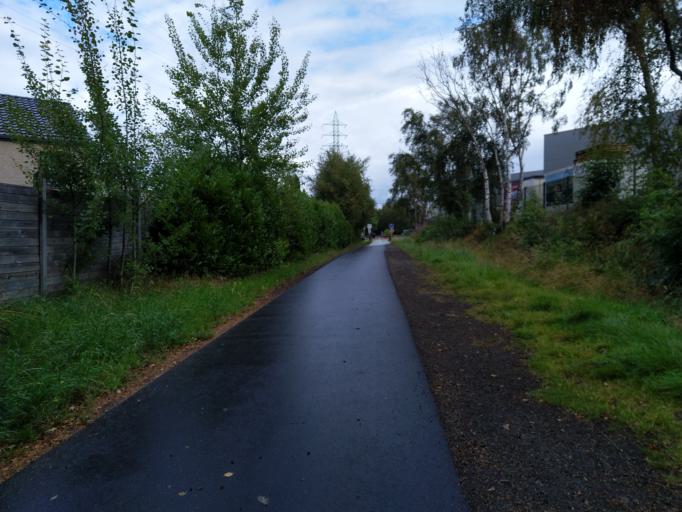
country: BE
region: Wallonia
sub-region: Province de Liege
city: Herve
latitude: 50.6503
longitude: 5.8086
